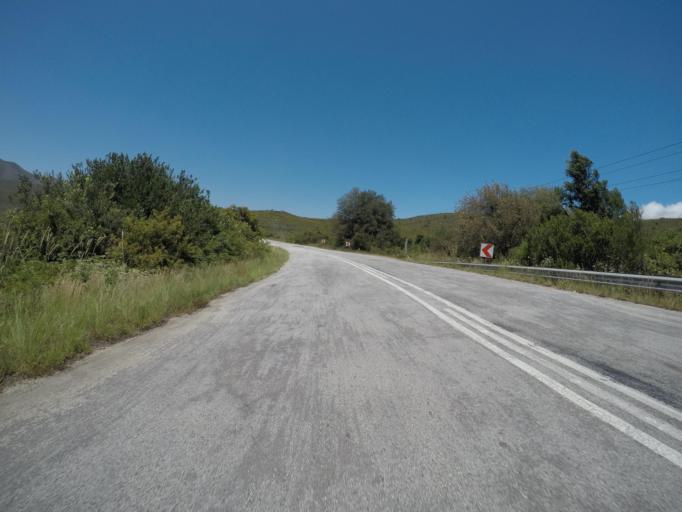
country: ZA
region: Eastern Cape
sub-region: Cacadu District Municipality
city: Kareedouw
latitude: -33.8863
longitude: 24.0777
